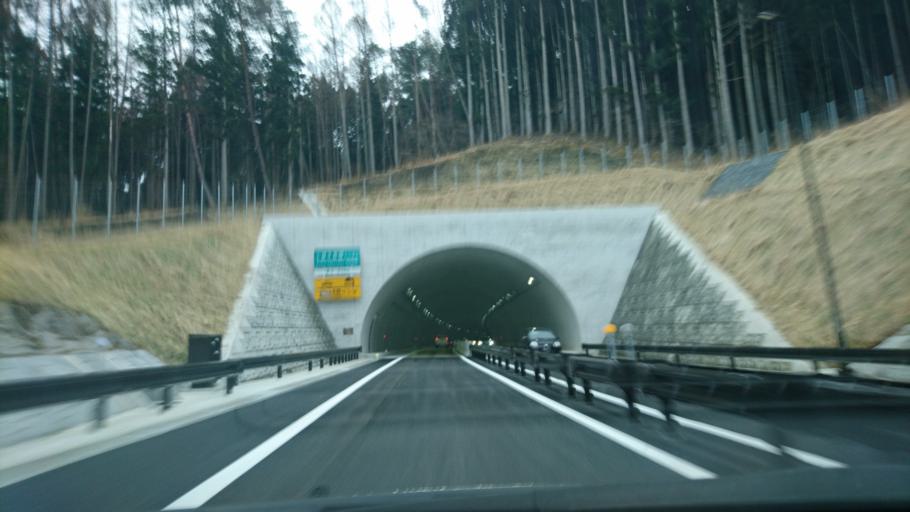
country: JP
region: Iwate
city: Ofunato
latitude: 38.9754
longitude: 141.6232
